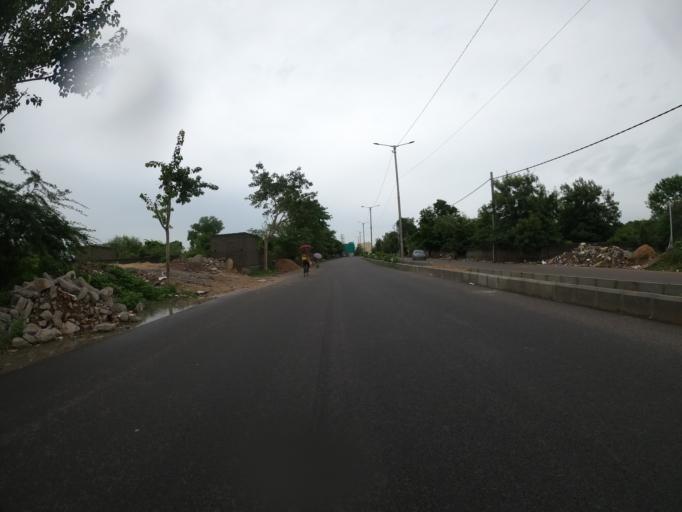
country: IN
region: Telangana
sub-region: Rangareddi
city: Kukatpalli
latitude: 17.4602
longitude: 78.3946
